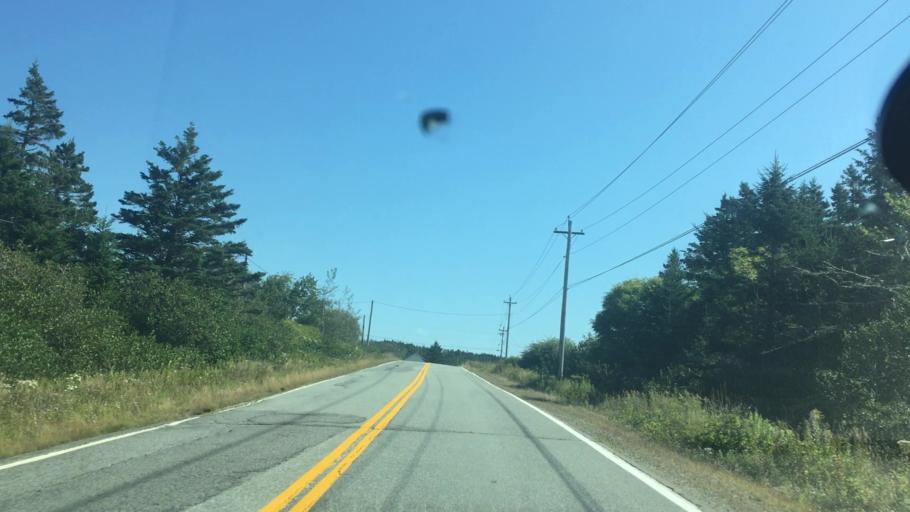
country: CA
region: Nova Scotia
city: New Glasgow
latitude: 44.9172
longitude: -62.3262
